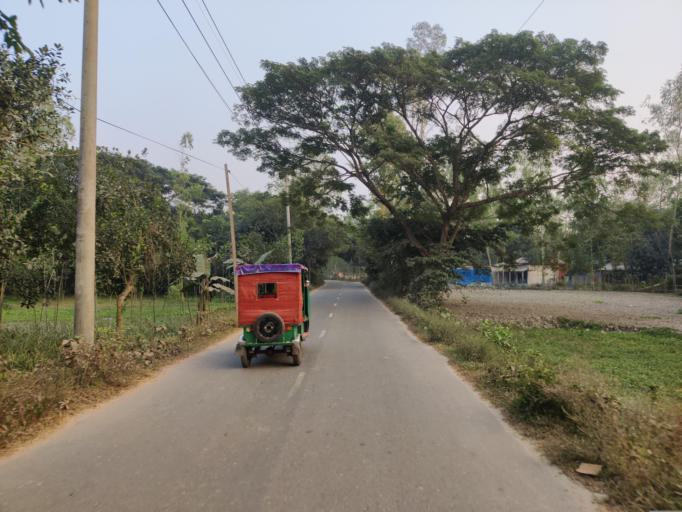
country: BD
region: Dhaka
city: Bajitpur
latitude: 24.1589
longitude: 90.7999
